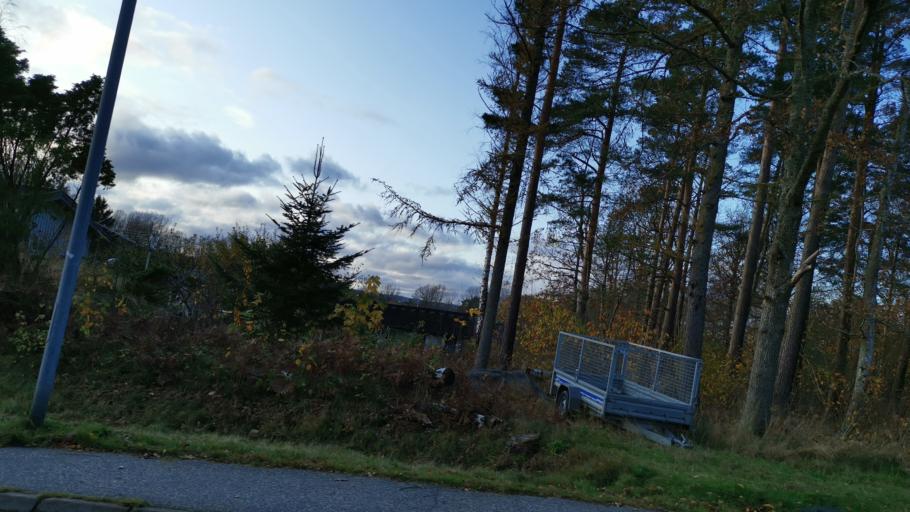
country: SE
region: Vaestra Goetaland
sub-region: Munkedals Kommun
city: Munkedal
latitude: 58.4614
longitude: 11.6650
